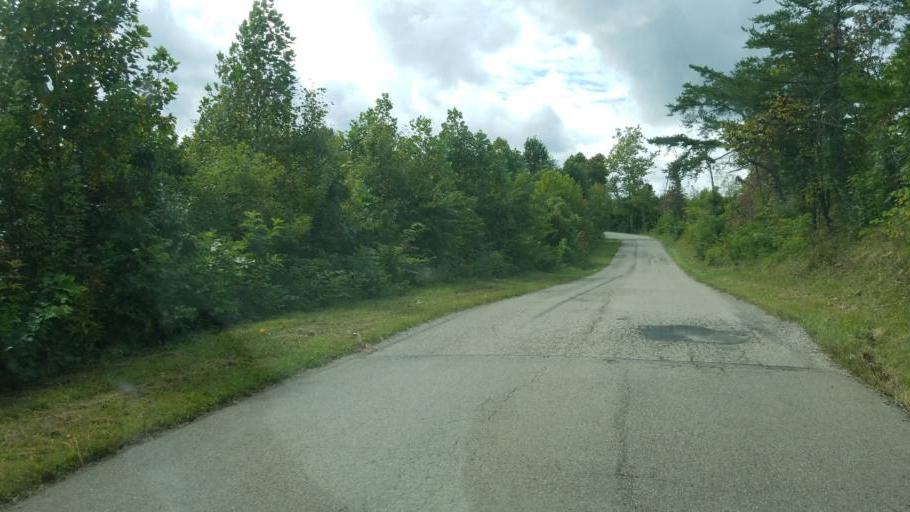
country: US
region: Ohio
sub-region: Jackson County
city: Oak Hill
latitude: 38.8945
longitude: -82.6334
